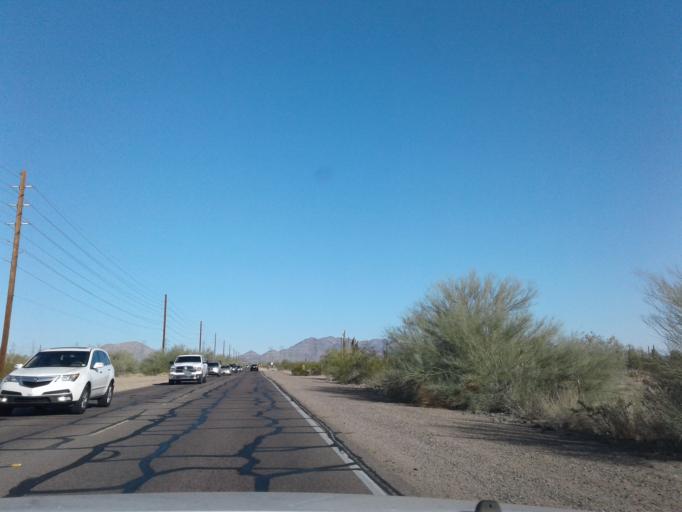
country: US
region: Arizona
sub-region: Maricopa County
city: Carefree
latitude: 33.6987
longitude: -111.9530
